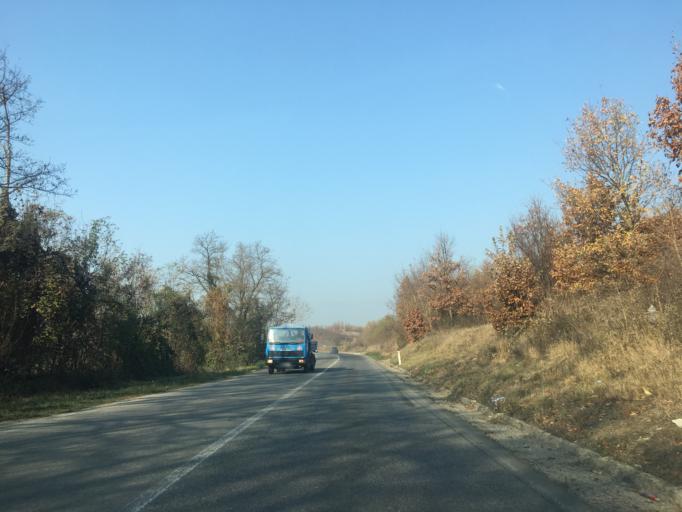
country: XK
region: Pec
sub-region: Komuna e Pejes
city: Kosuriq
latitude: 42.6391
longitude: 20.4278
